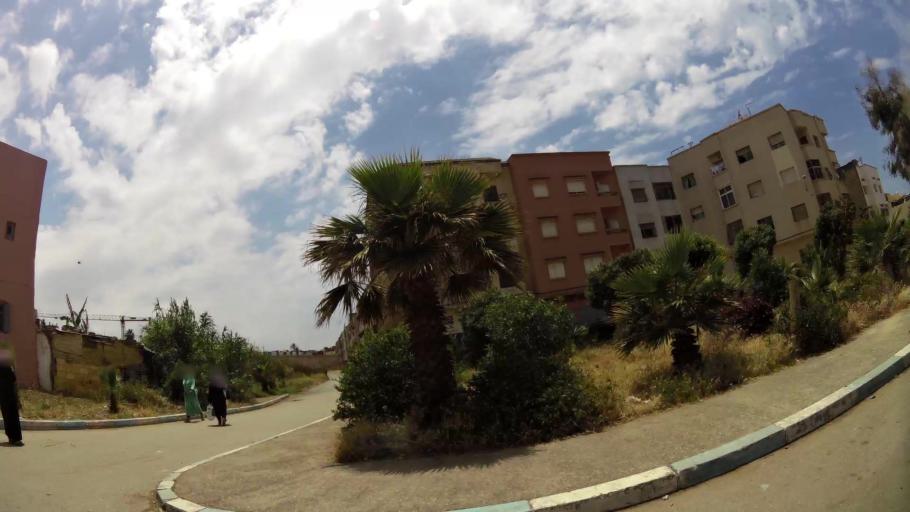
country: MA
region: Rabat-Sale-Zemmour-Zaer
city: Sale
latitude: 34.0469
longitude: -6.8237
